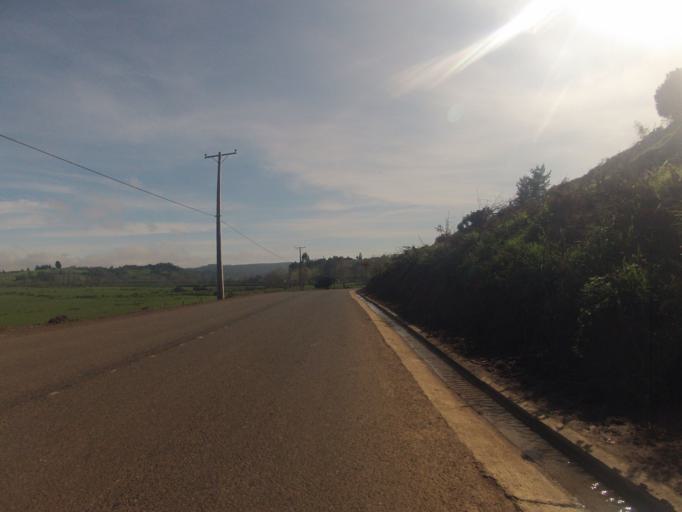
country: CL
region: Araucania
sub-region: Provincia de Cautin
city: Temuco
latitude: -38.7131
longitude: -72.5993
